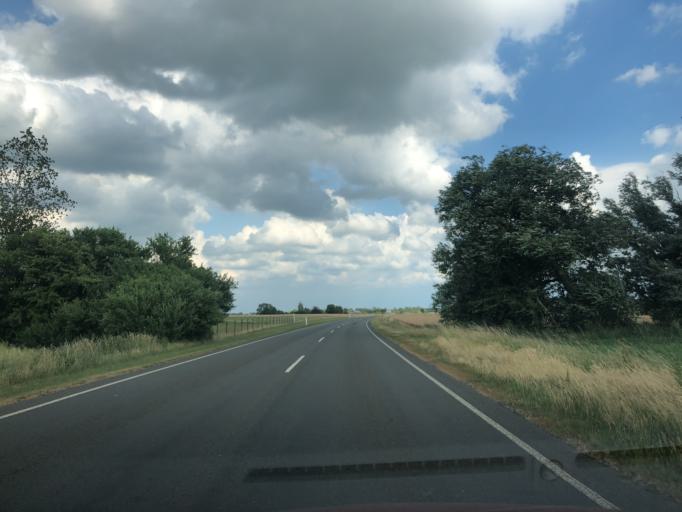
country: DK
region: Zealand
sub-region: Stevns Kommune
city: Harlev
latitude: 55.3149
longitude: 12.2119
